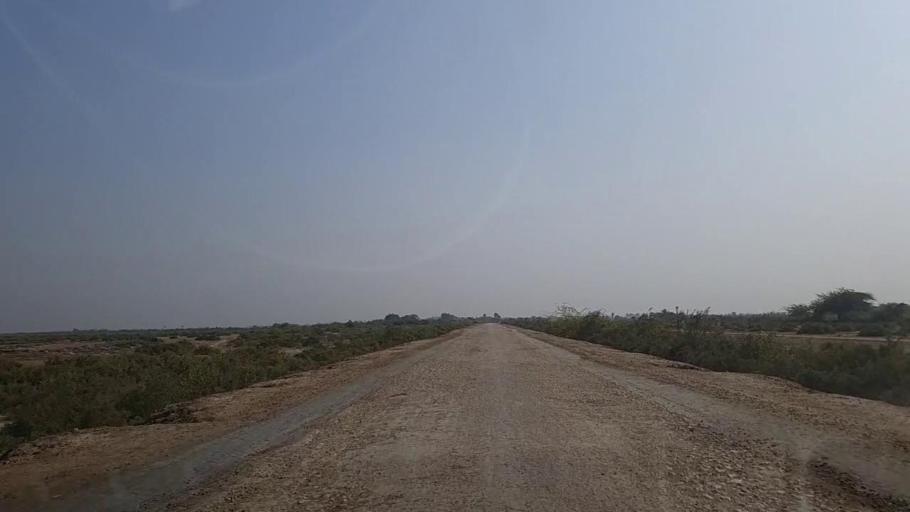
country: PK
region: Sindh
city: Keti Bandar
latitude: 24.2530
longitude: 67.6261
